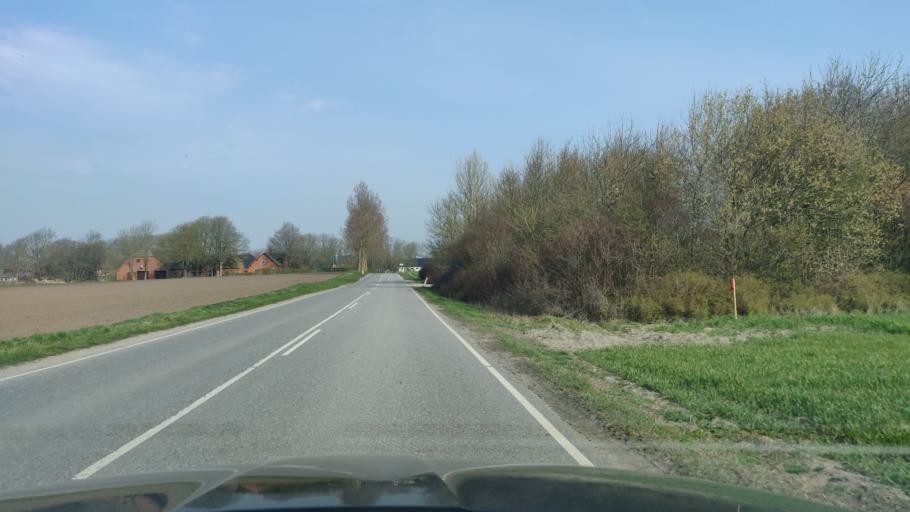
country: DK
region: South Denmark
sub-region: Nordfyns Kommune
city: Sonderso
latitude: 55.5081
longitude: 10.2502
